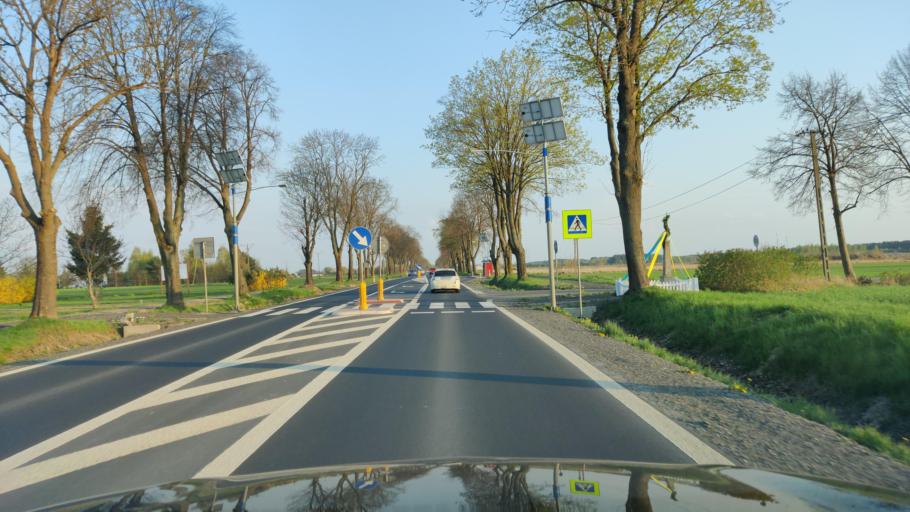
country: PL
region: Masovian Voivodeship
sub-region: Powiat pultuski
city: Zatory
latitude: 52.6162
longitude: 21.1035
